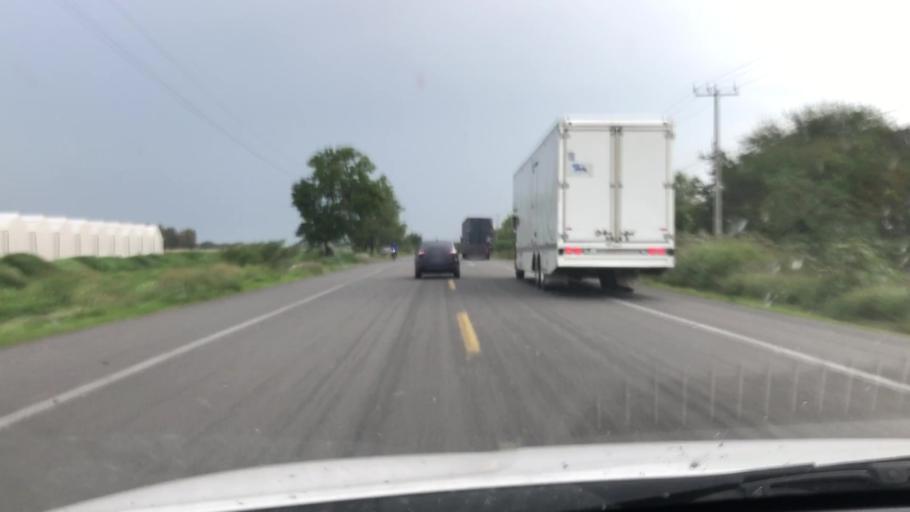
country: MX
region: Michoacan
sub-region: Vista Hermosa
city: Los Pilares
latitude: 20.2754
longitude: -102.3966
